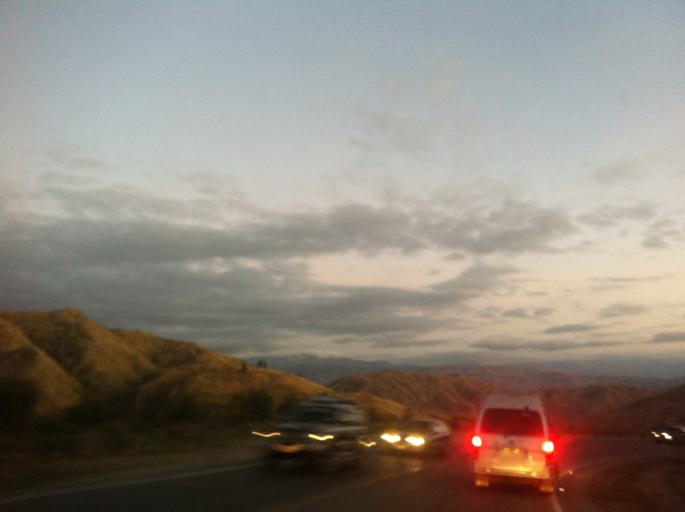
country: BO
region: Cochabamba
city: Irpa Irpa
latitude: -17.6610
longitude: -66.4280
